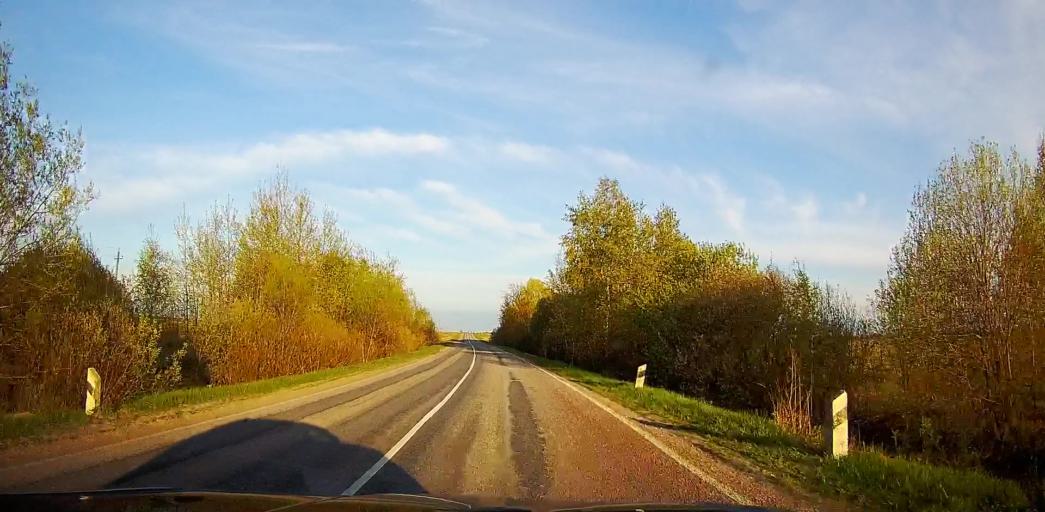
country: RU
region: Moskovskaya
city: Bronnitsy
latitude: 55.2753
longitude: 38.2262
